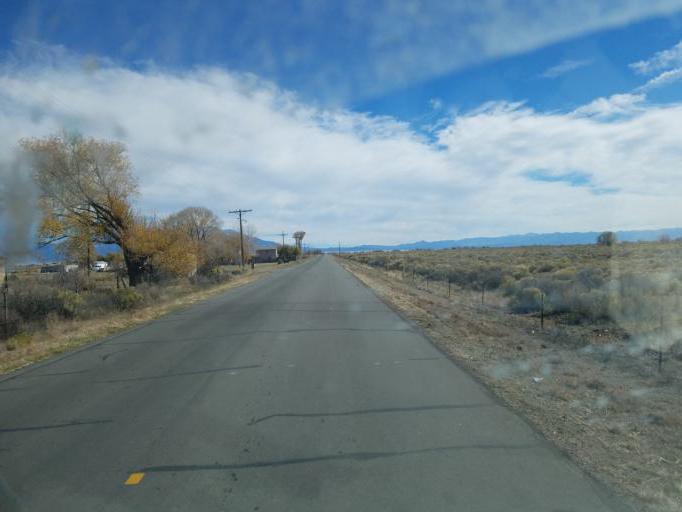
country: US
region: Colorado
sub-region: Alamosa County
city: Alamosa East
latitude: 37.5026
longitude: -105.8524
